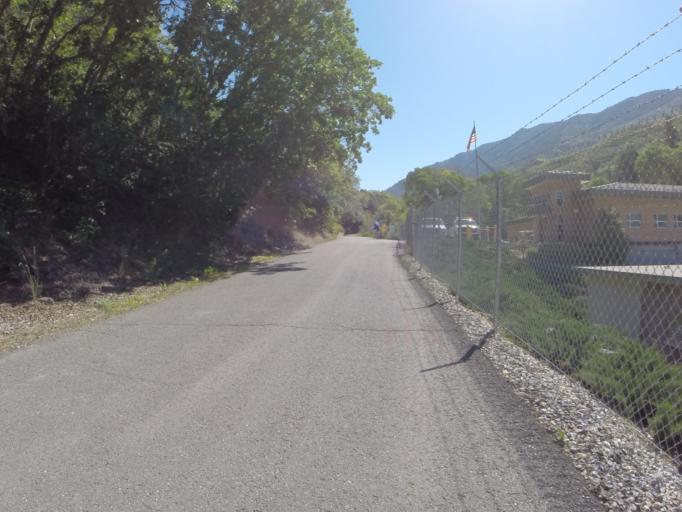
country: US
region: Utah
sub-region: Salt Lake County
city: Salt Lake City
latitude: 40.8153
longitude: -111.8319
